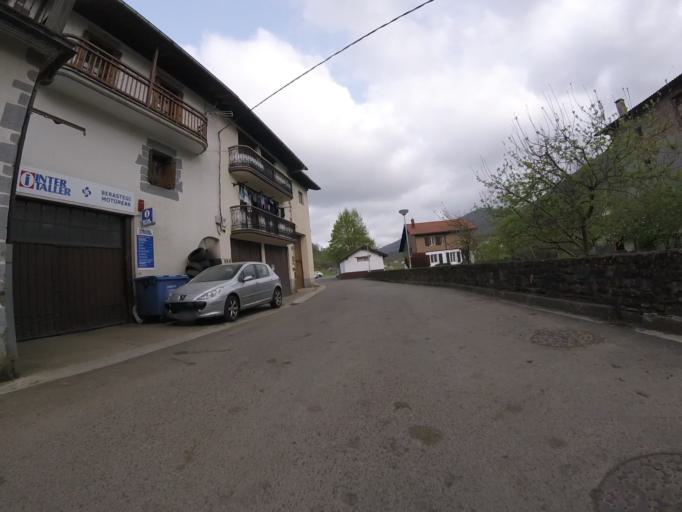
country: ES
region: Basque Country
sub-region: Provincia de Guipuzcoa
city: Berastegui
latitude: 43.1241
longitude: -1.9845
